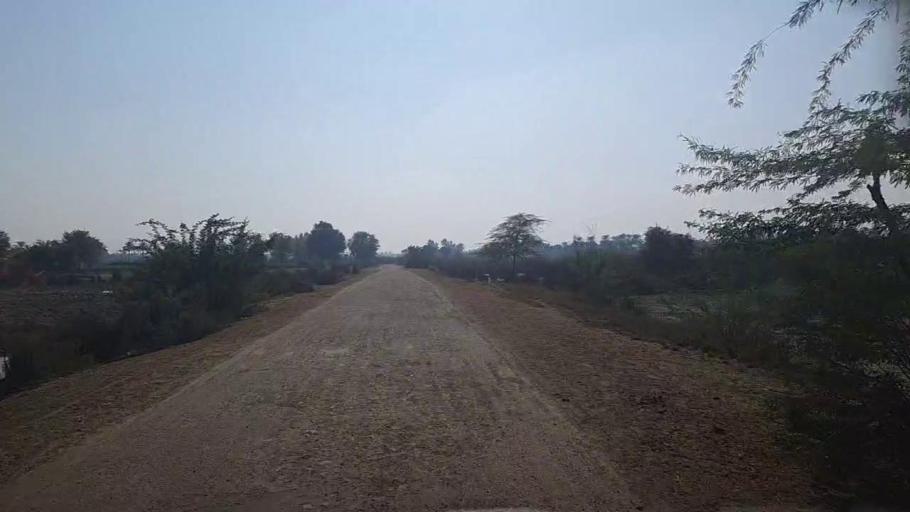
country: PK
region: Sindh
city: Kot Diji
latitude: 27.4267
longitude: 68.7373
